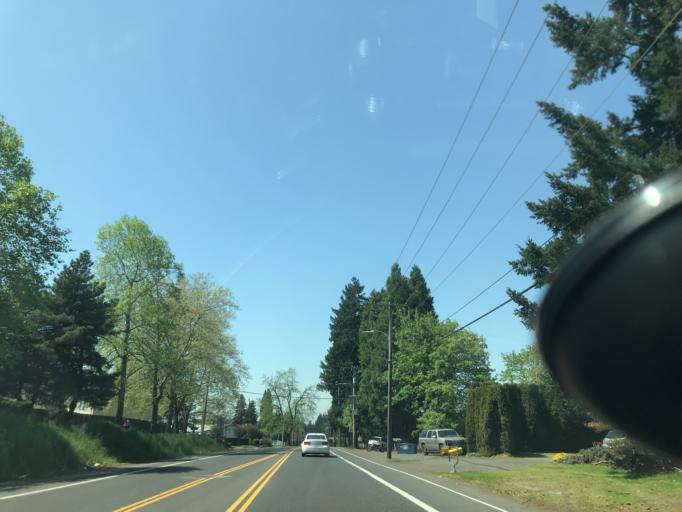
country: US
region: Oregon
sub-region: Multnomah County
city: Gresham
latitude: 45.4936
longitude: -122.4909
